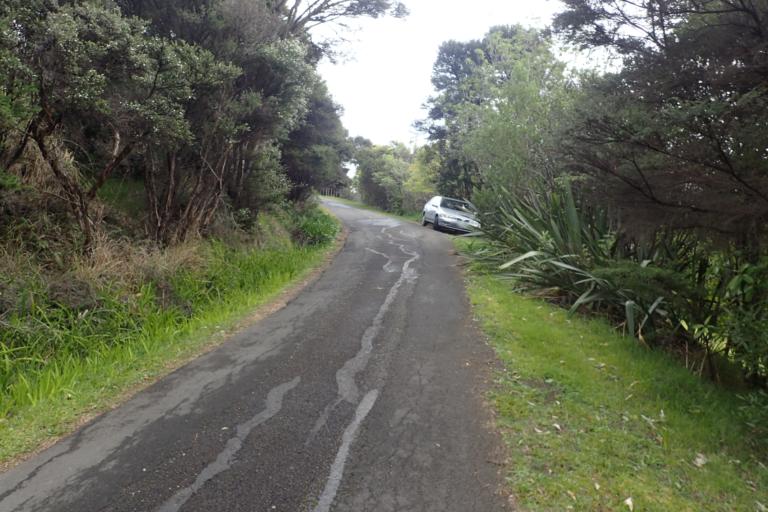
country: NZ
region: Auckland
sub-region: Auckland
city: Pakuranga
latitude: -36.7909
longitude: 175.0053
